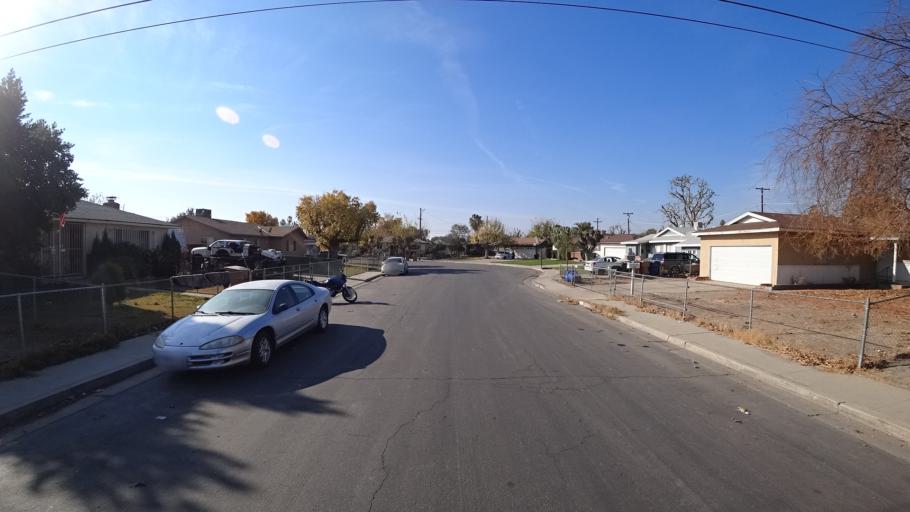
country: US
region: California
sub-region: Kern County
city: Bakersfield
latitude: 35.3273
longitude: -119.0075
